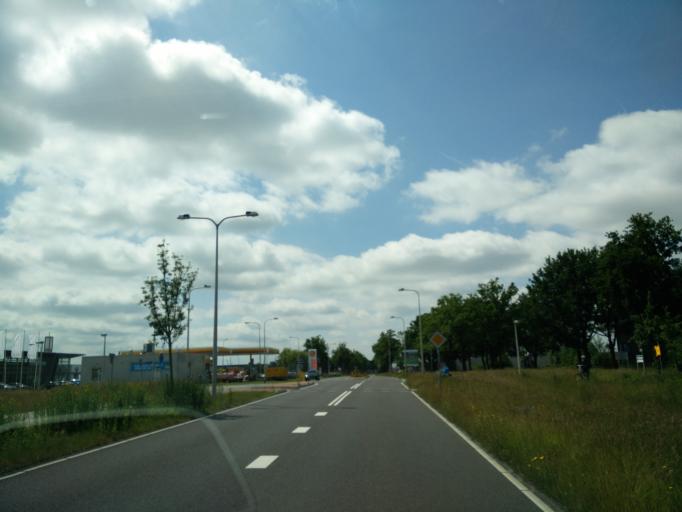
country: NL
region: Drenthe
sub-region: Gemeente Assen
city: Assen
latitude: 53.0100
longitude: 6.5711
